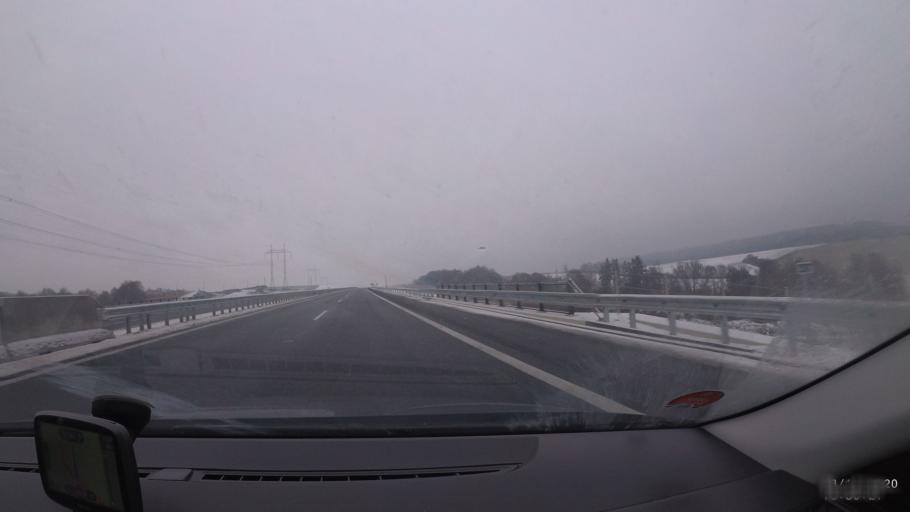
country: CZ
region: Central Bohemia
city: Revnicov
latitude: 50.1776
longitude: 13.7834
